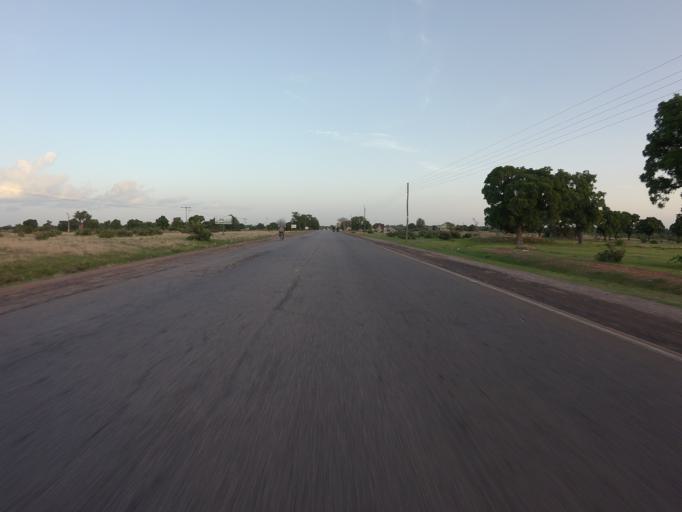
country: GH
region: Upper East
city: Navrongo
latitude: 10.9410
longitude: -1.0918
